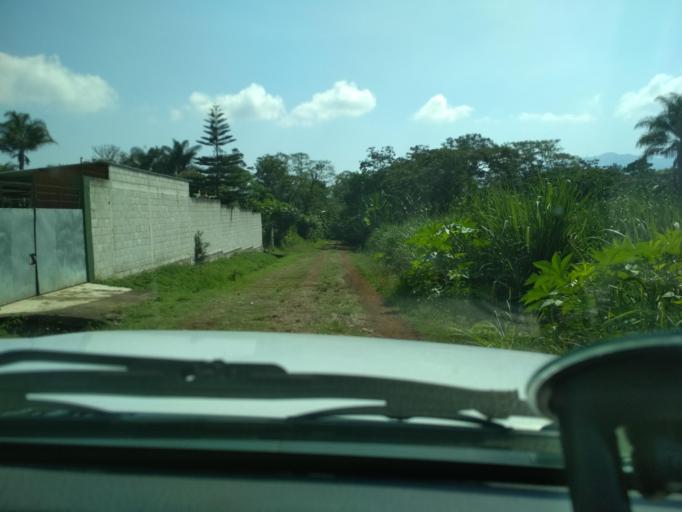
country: MX
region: Veracruz
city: Monte Blanco
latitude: 18.9793
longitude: -97.0111
